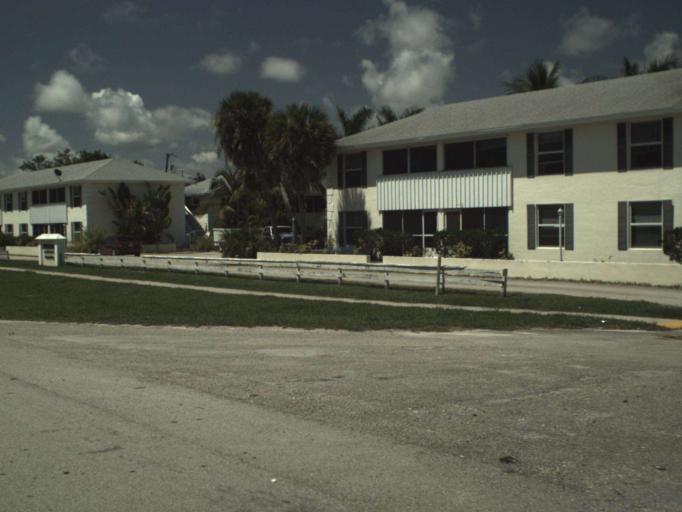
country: US
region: Florida
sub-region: Indian River County
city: Vero Beach
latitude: 27.6449
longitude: -80.3815
